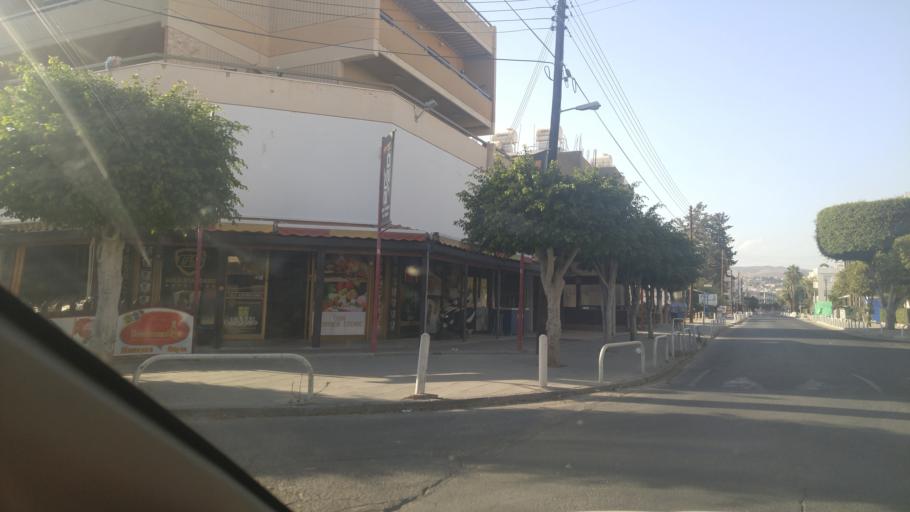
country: CY
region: Limassol
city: Mouttagiaka
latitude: 34.6982
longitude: 33.0924
